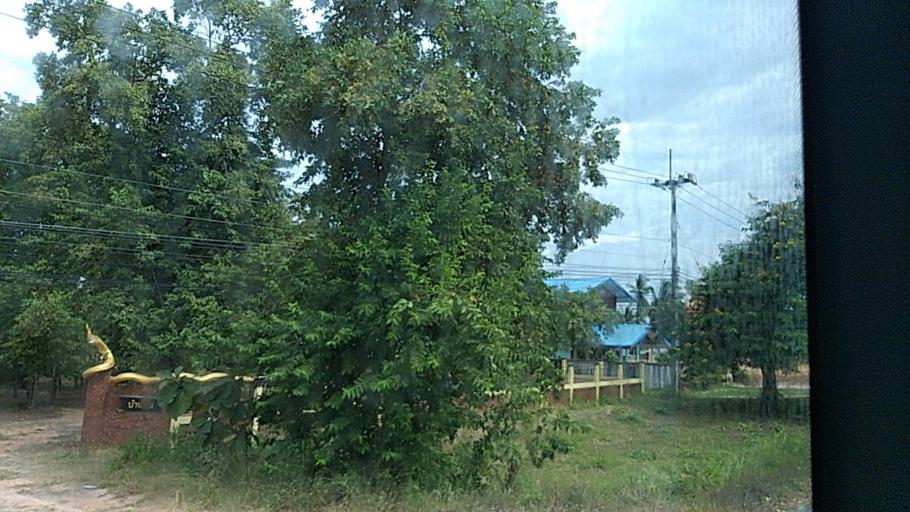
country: TH
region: Maha Sarakham
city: Maha Sarakham
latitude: 16.1523
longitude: 103.3781
